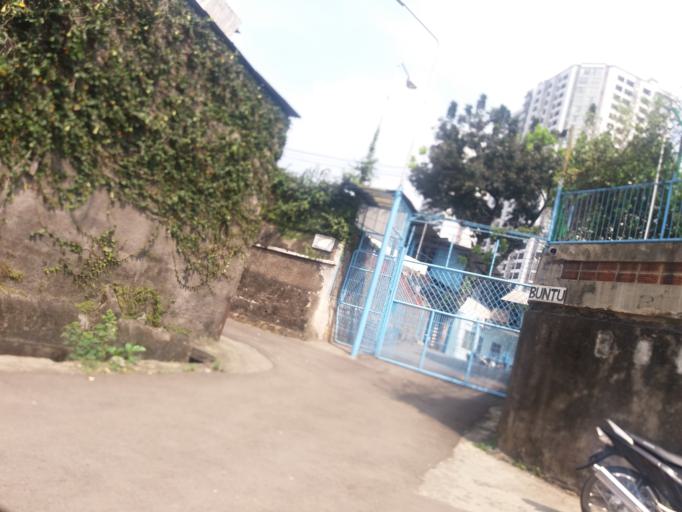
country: ID
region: Jakarta Raya
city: Jakarta
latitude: -6.2244
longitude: 106.8189
